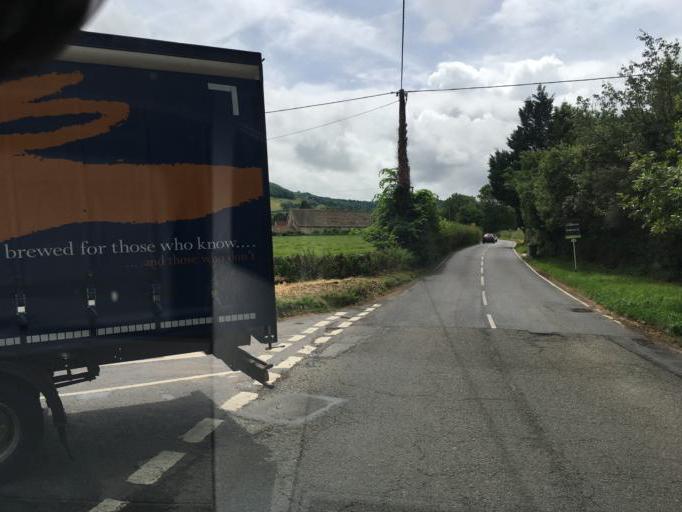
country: GB
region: England
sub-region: Gloucestershire
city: Stonehouse
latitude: 51.7270
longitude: -2.3118
